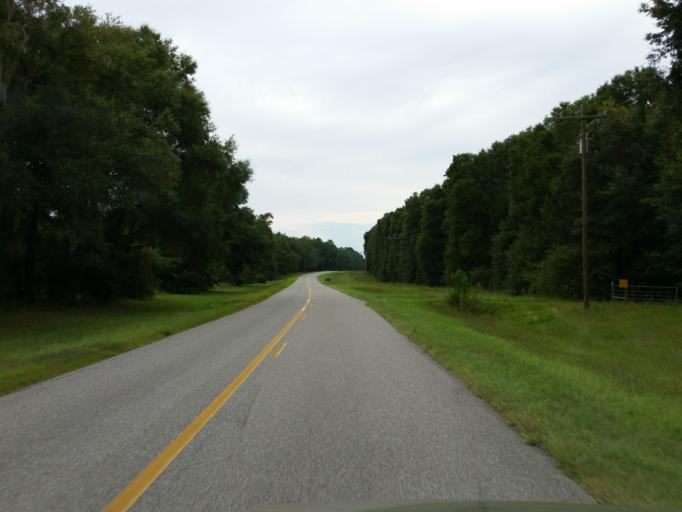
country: US
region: Florida
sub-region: Alachua County
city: High Springs
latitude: 29.9519
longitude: -82.5194
